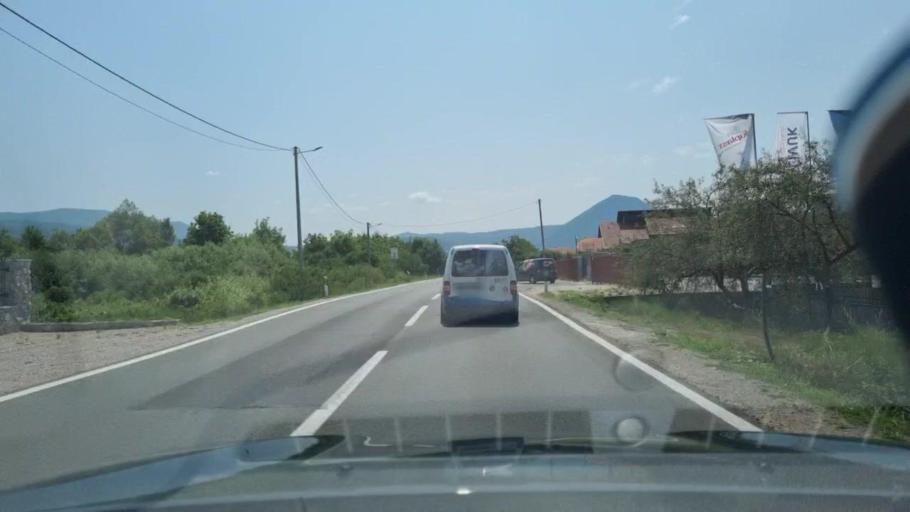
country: BA
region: Federation of Bosnia and Herzegovina
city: Bihac
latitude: 44.7882
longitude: 15.9309
